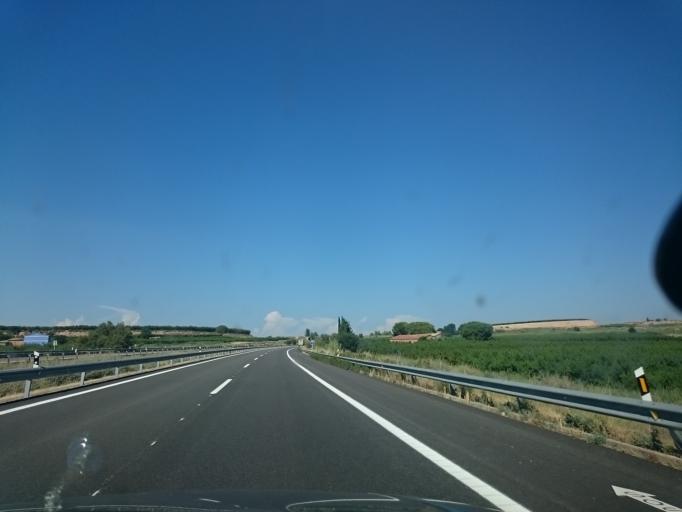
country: ES
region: Catalonia
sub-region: Provincia de Lleida
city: Seros
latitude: 41.5022
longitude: 0.4041
